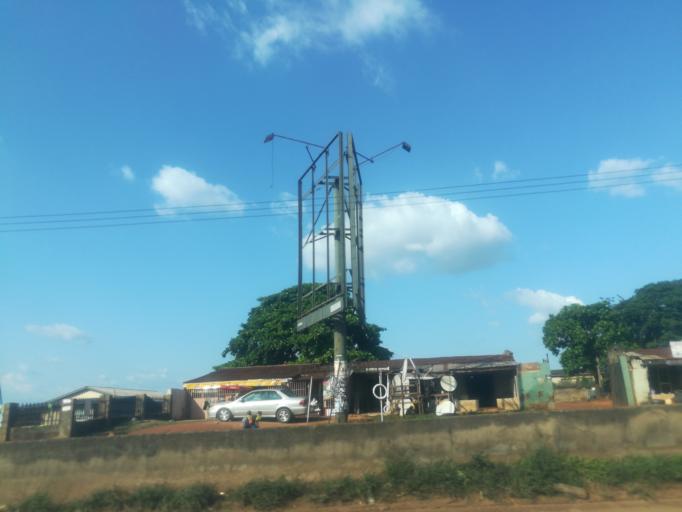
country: NG
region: Oyo
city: Ibadan
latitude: 7.3905
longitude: 3.9750
